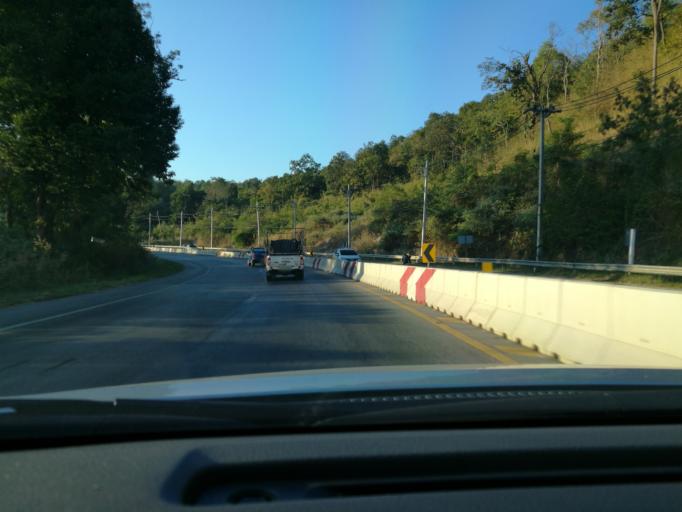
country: TH
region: Phitsanulok
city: Wang Thong
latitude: 16.8529
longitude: 100.5151
